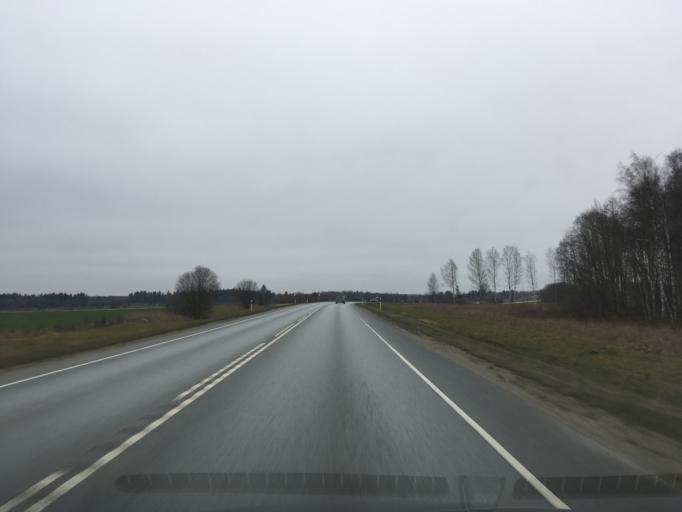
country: EE
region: Laeaene-Virumaa
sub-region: Viru-Nigula vald
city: Kunda
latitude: 59.4189
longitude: 26.6563
